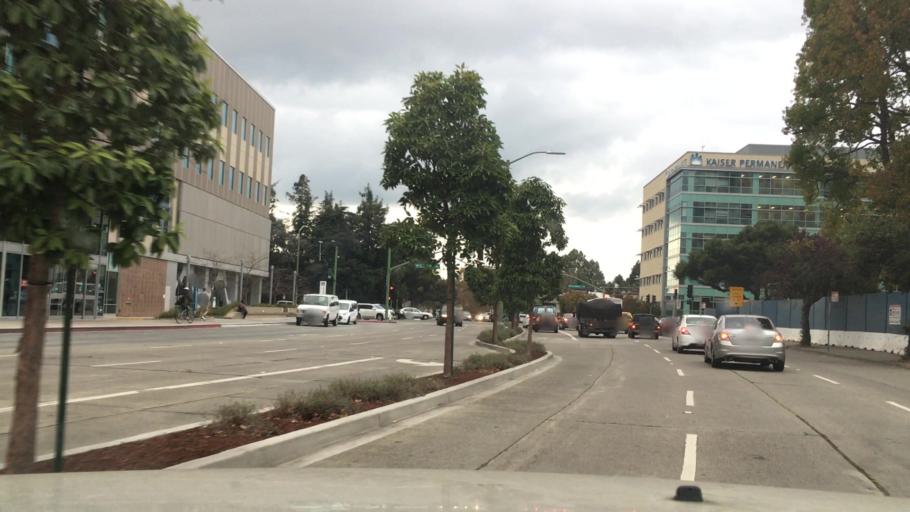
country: US
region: California
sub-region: Alameda County
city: Oakland
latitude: 37.8239
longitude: -122.2576
